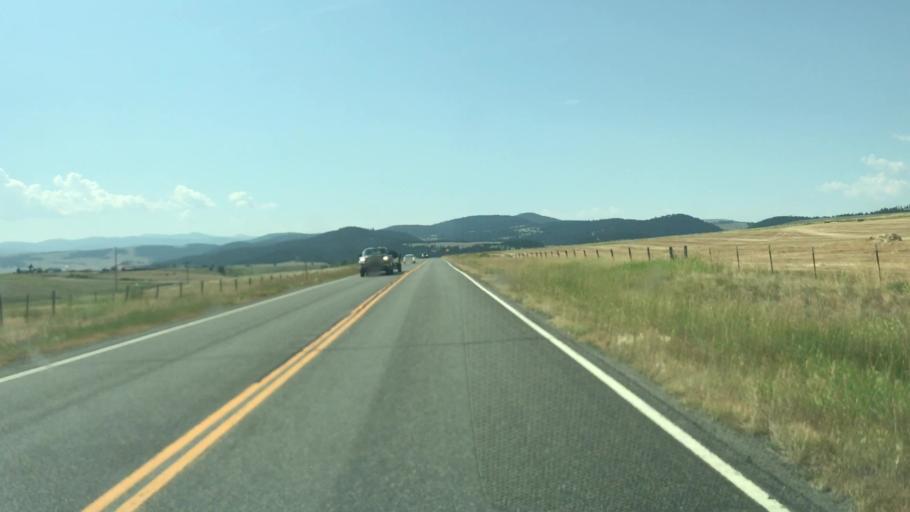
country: US
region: Montana
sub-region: Powell County
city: Deer Lodge
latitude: 46.6380
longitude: -112.6304
